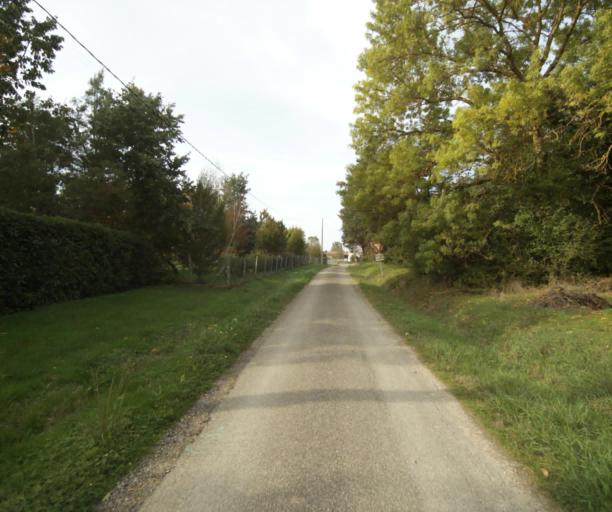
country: FR
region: Midi-Pyrenees
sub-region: Departement du Tarn-et-Garonne
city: Campsas
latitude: 43.9057
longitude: 1.3349
